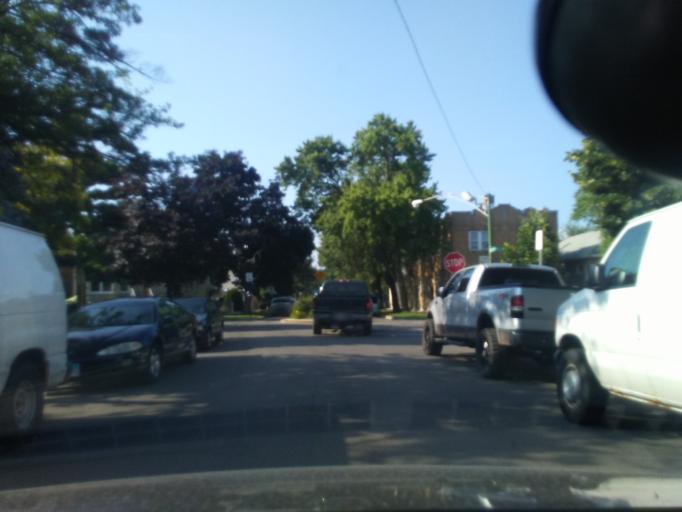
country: US
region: Illinois
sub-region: Cook County
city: Elmwood Park
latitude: 41.9353
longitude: -87.7590
